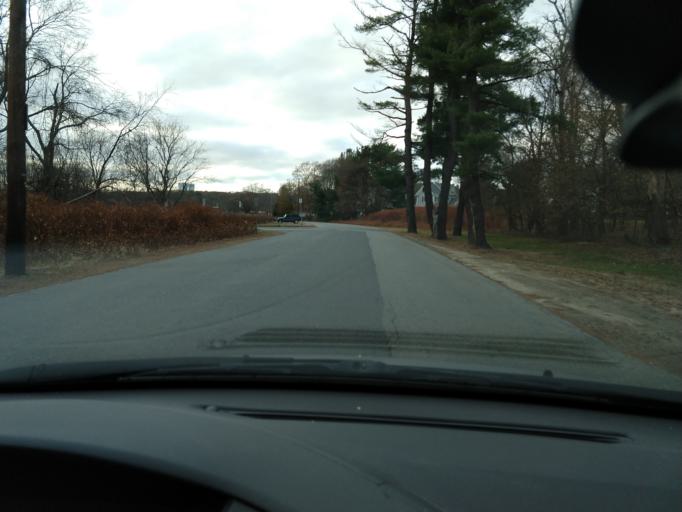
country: US
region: Massachusetts
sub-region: Middlesex County
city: Lexington
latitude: 42.4452
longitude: -71.2314
